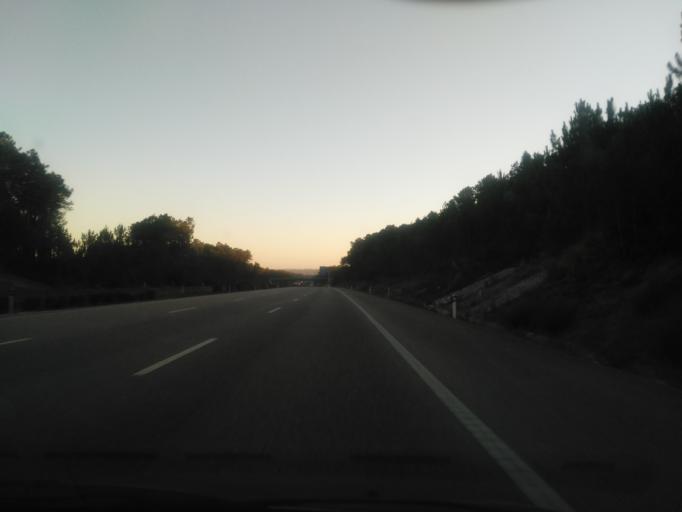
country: PT
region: Leiria
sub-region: Alcobaca
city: Pataias
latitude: 39.6605
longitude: -8.9584
